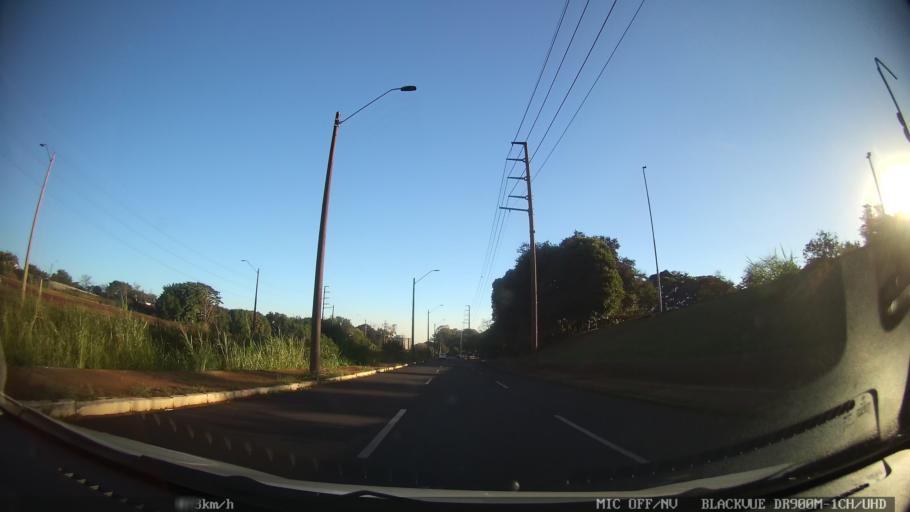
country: BR
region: Sao Paulo
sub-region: Araraquara
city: Araraquara
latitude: -21.8083
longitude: -48.1748
